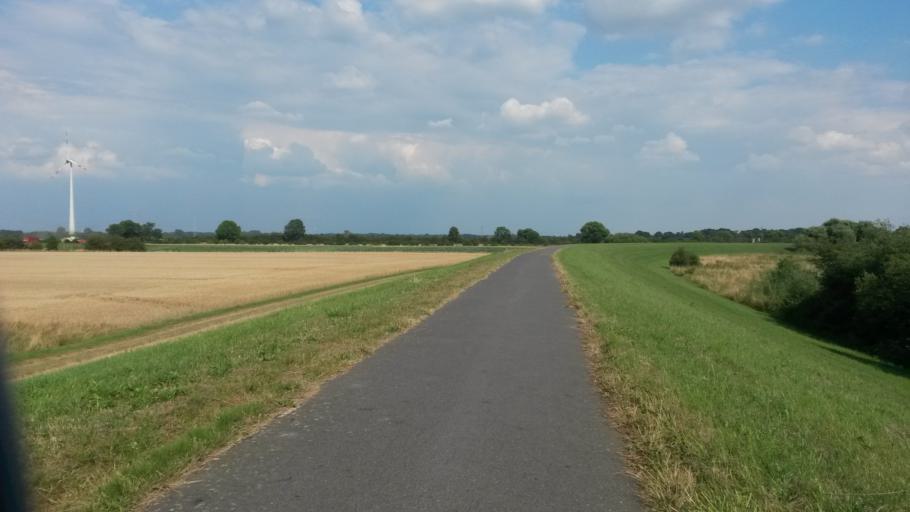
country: DE
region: Lower Saxony
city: Riede
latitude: 53.0171
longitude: 8.9186
